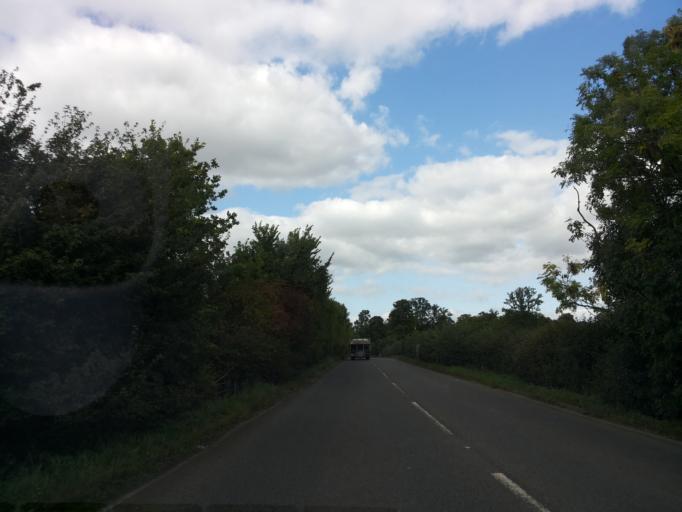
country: GB
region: England
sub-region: Bath and North East Somerset
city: Hinton Charterhouse
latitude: 51.3026
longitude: -2.3058
